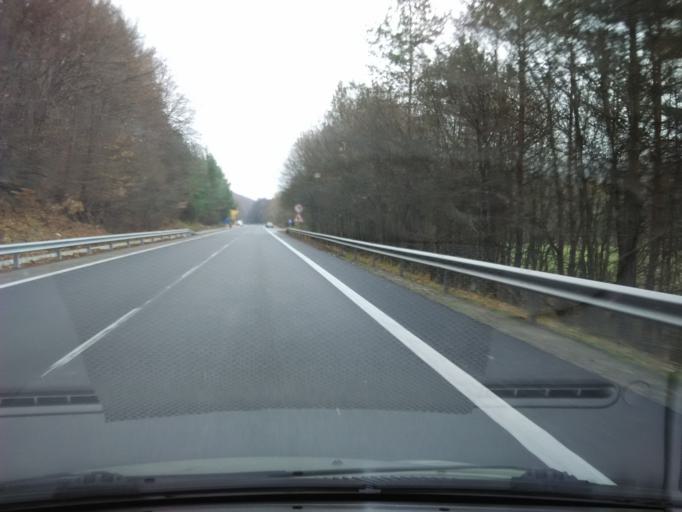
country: SK
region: Banskobystricky
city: Ziar nad Hronom
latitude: 48.6215
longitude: 18.8965
